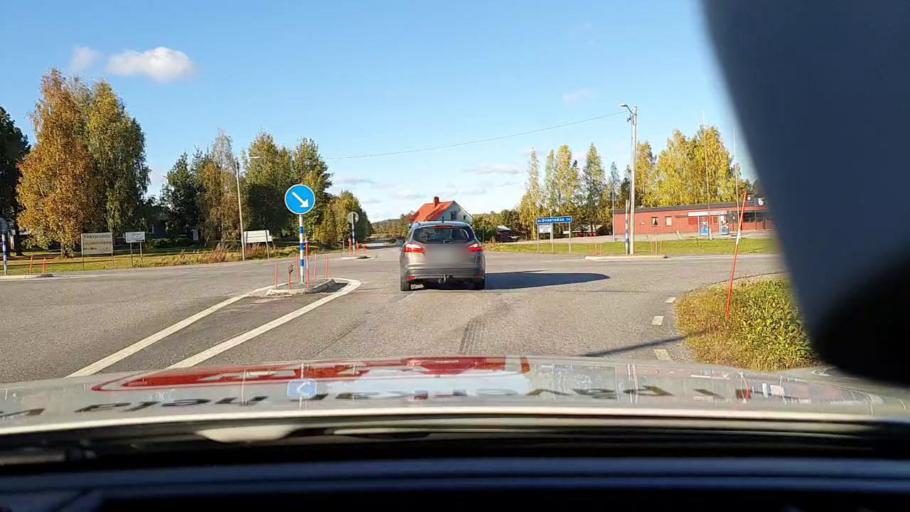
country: SE
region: Norrbotten
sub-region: Pitea Kommun
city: Norrfjarden
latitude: 65.5163
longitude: 21.4950
